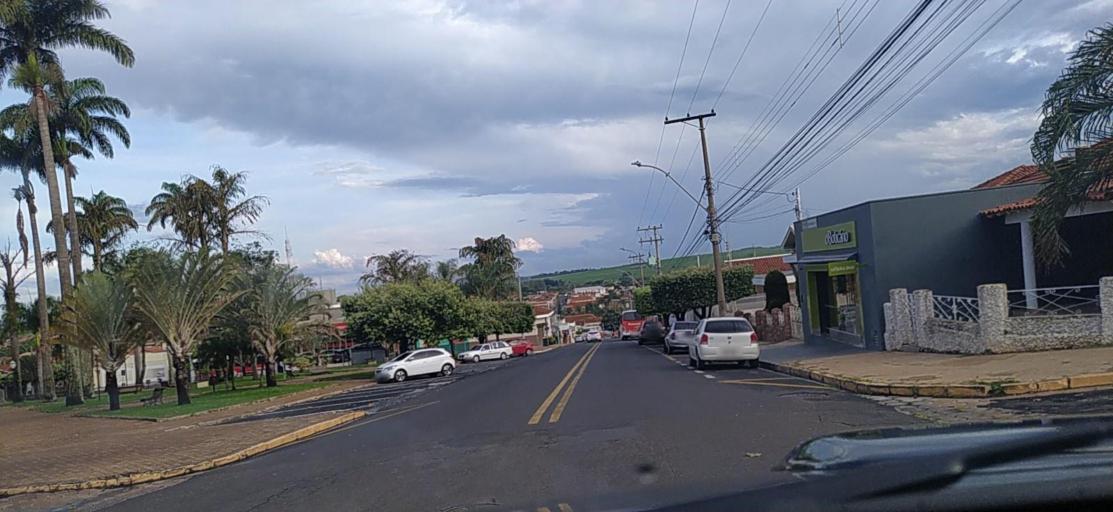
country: BR
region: Sao Paulo
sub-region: Pindorama
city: Pindorama
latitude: -21.1862
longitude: -48.9090
